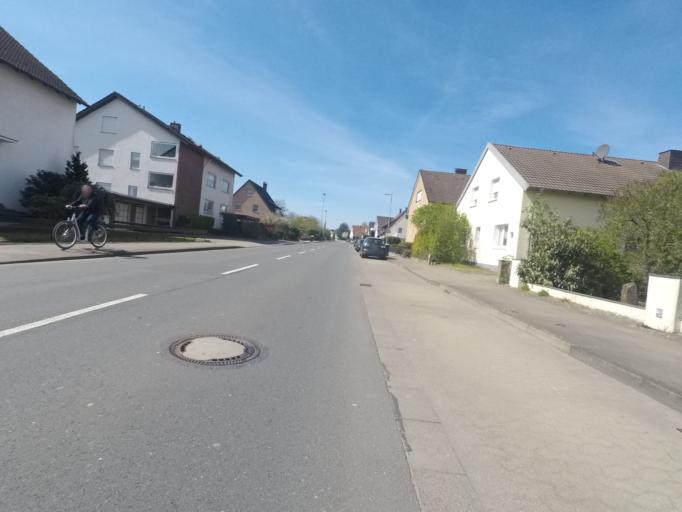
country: DE
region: North Rhine-Westphalia
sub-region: Regierungsbezirk Detmold
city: Herford
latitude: 52.0558
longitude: 8.6374
